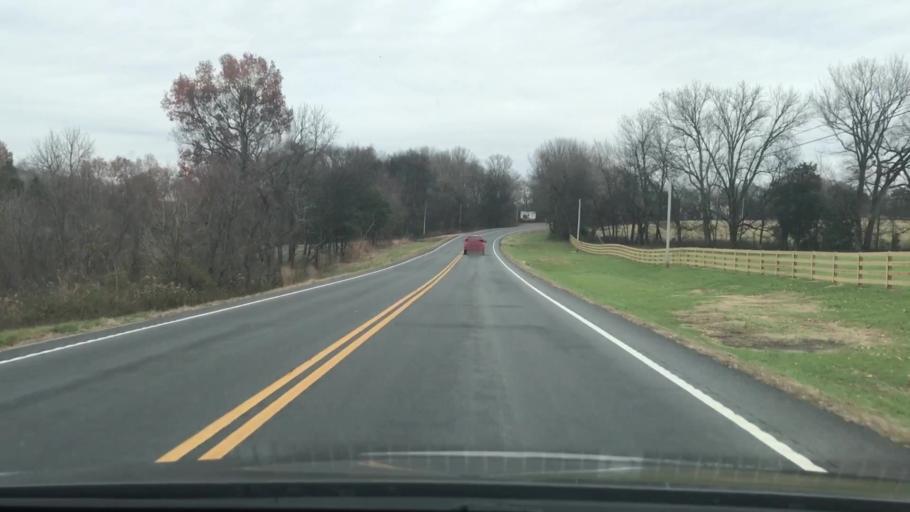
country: US
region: Tennessee
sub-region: Trousdale County
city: Hartsville
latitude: 36.3987
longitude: -86.2244
